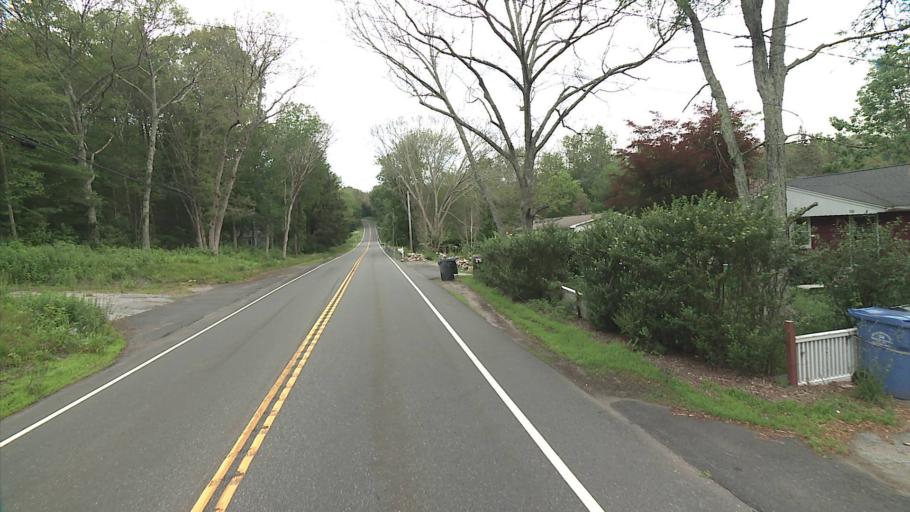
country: US
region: Connecticut
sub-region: New London County
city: Ledyard Center
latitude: 41.4613
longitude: -72.0177
